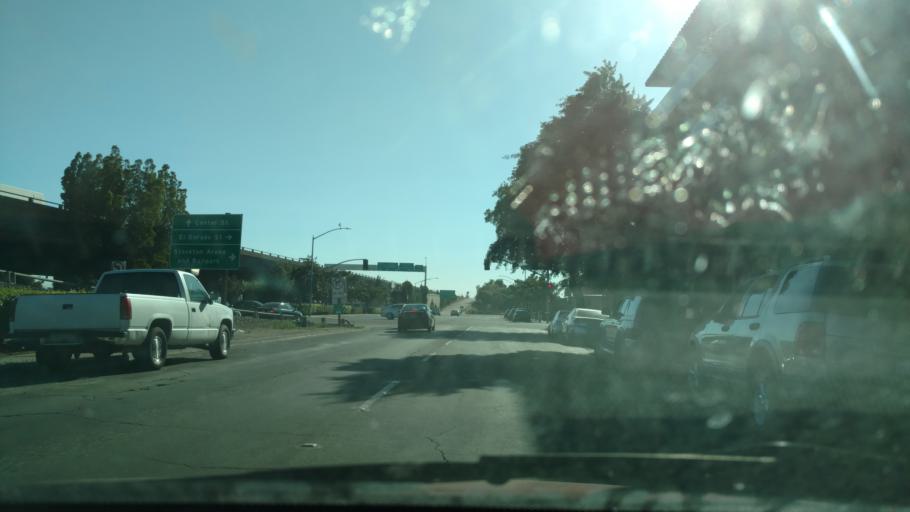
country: US
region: California
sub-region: San Joaquin County
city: Stockton
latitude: 37.9509
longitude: -121.2886
